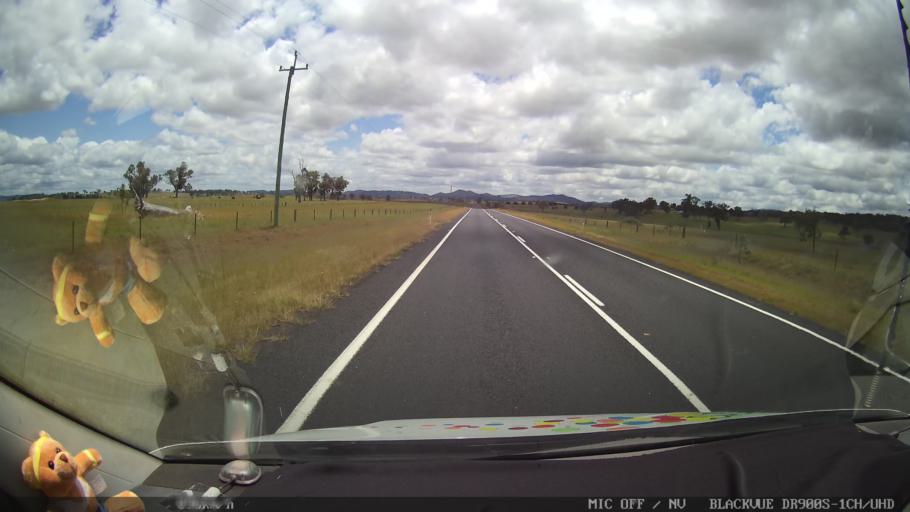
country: AU
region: New South Wales
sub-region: Glen Innes Severn
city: Glen Innes
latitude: -29.4235
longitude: 151.8597
